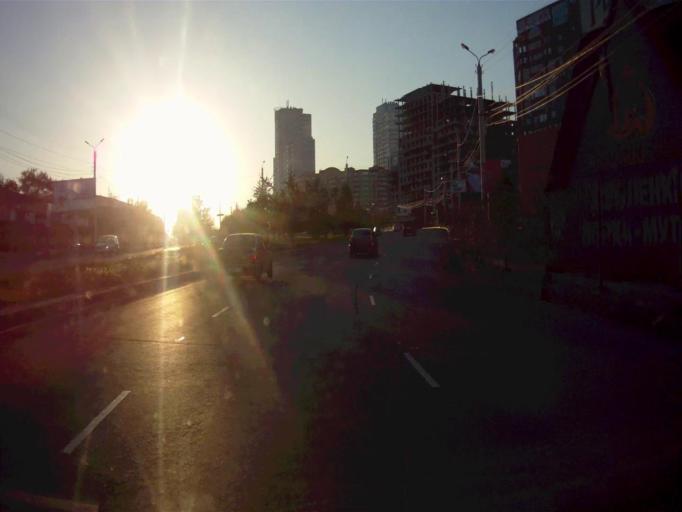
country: RU
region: Chelyabinsk
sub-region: Gorod Chelyabinsk
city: Chelyabinsk
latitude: 55.1736
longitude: 61.3975
